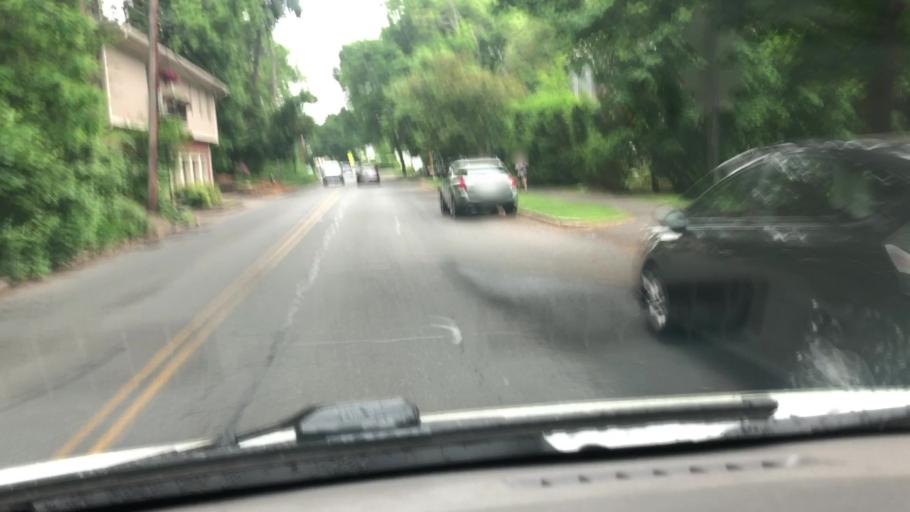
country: US
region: Massachusetts
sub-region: Hampshire County
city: Northampton
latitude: 42.3223
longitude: -72.6347
